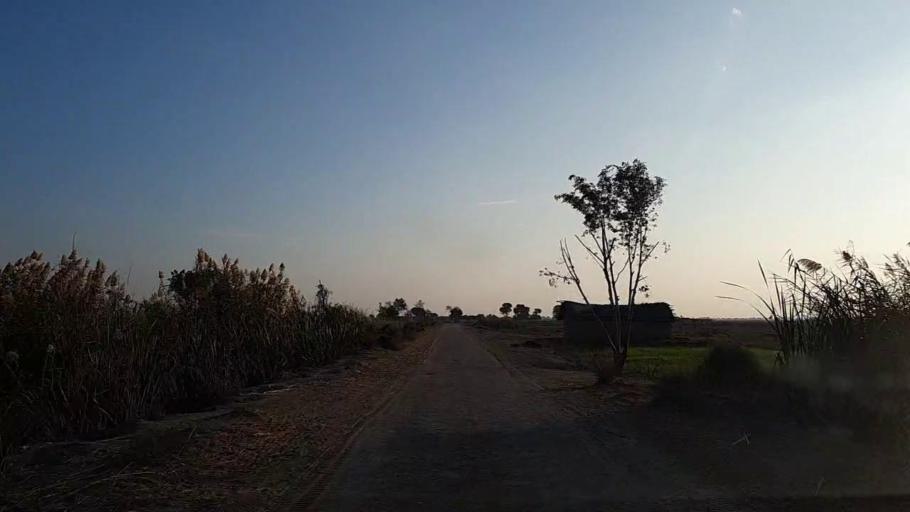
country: PK
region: Sindh
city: Sanghar
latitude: 26.2682
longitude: 68.9818
